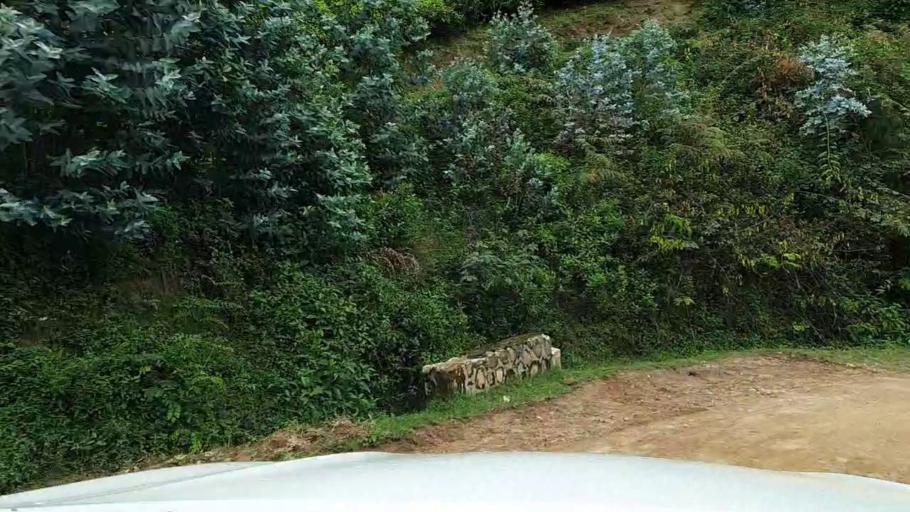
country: RW
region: Western Province
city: Kibuye
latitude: -2.2899
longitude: 29.3730
